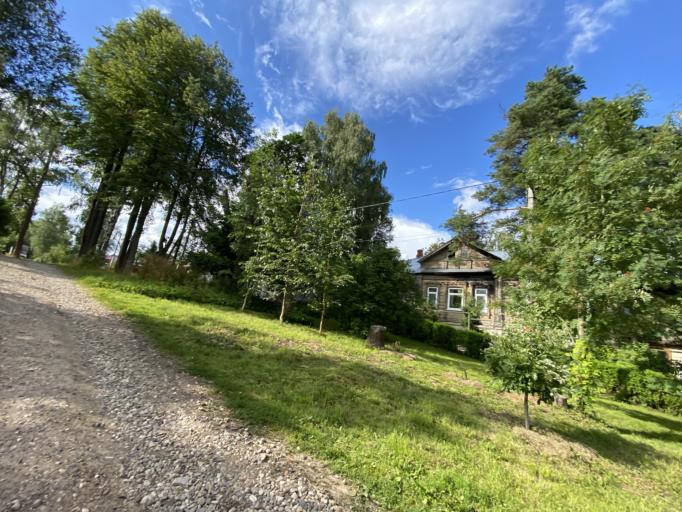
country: RU
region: Moskovskaya
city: Sergiyev Posad
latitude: 56.3086
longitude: 38.1552
